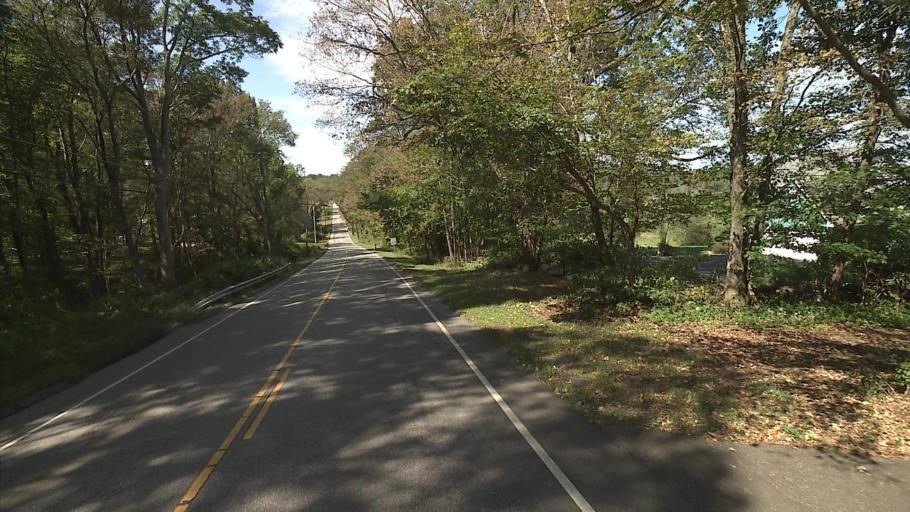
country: US
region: Connecticut
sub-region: Tolland County
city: South Coventry
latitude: 41.6916
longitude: -72.2903
